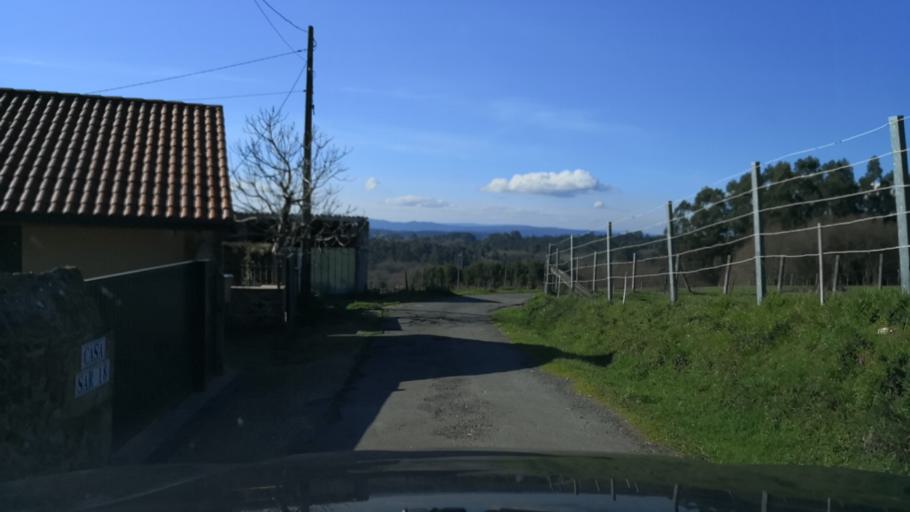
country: ES
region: Galicia
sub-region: Provincia da Coruna
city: Ribeira
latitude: 42.7073
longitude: -8.4281
